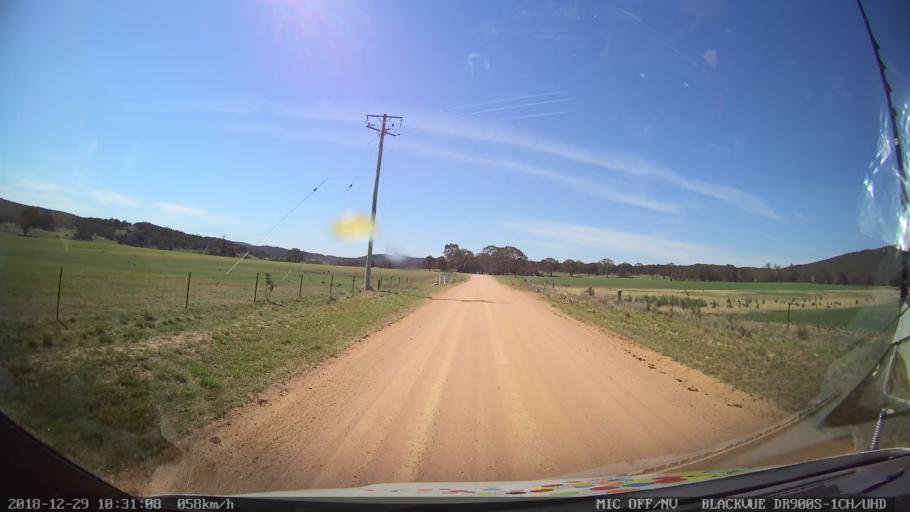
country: AU
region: New South Wales
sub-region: Yass Valley
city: Gundaroo
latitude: -34.9657
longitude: 149.4558
